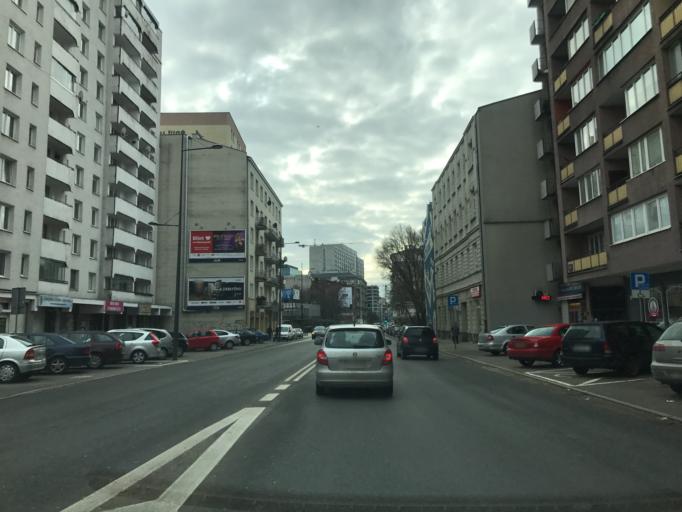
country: PL
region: Masovian Voivodeship
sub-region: Warszawa
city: Wola
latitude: 52.2384
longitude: 20.9881
